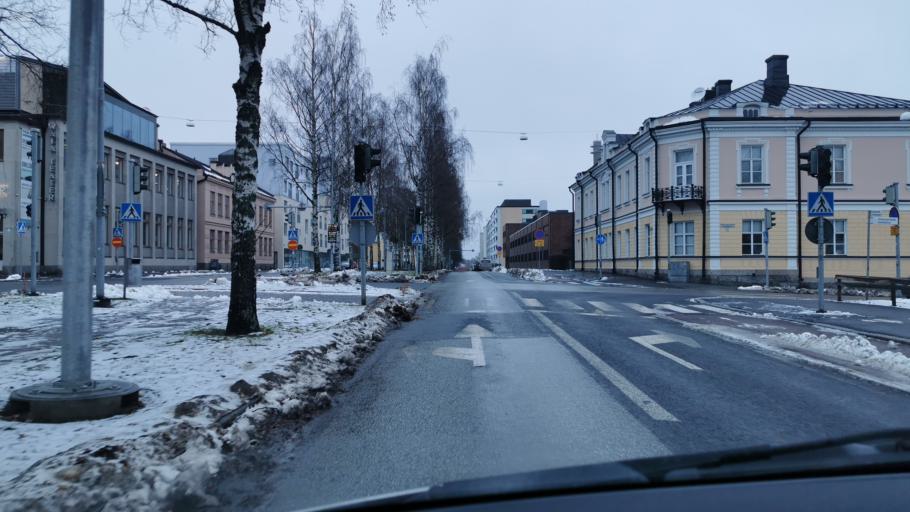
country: FI
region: Ostrobothnia
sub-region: Vaasa
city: Vaasa
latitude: 63.0966
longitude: 21.6086
